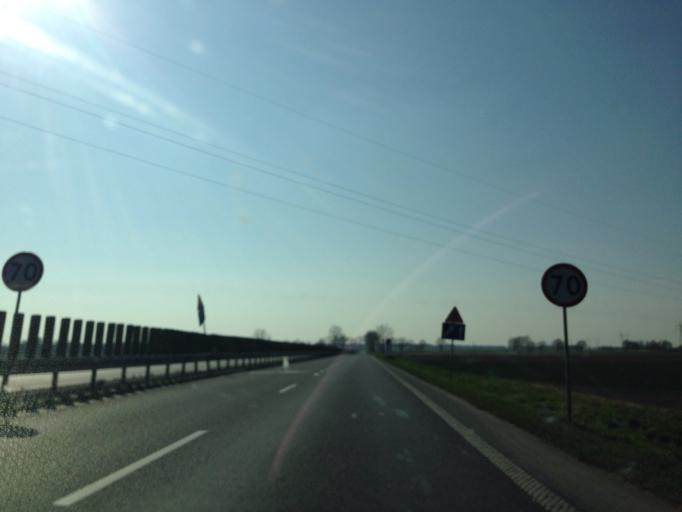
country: PL
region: Lower Silesian Voivodeship
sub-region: Powiat olesnicki
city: Dobroszyce
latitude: 51.1983
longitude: 17.3051
